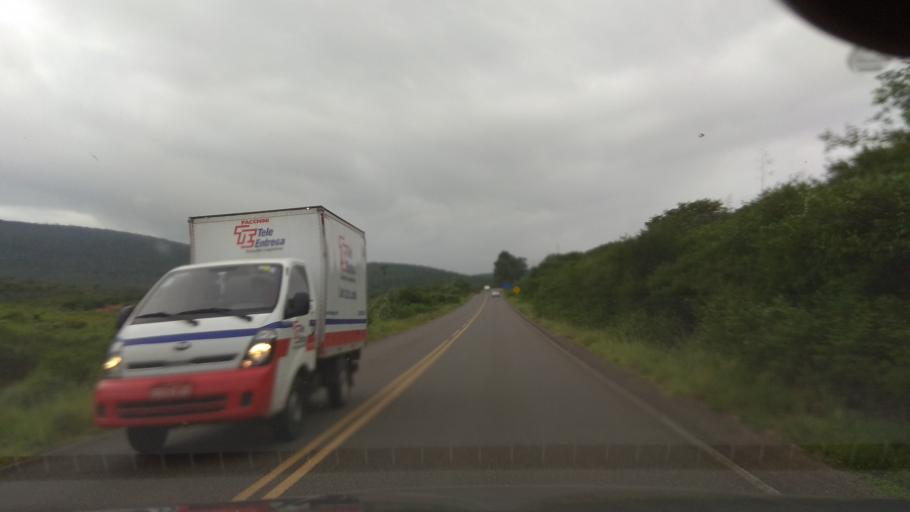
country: BR
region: Bahia
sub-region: Santa Ines
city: Santa Ines
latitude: -13.2748
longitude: -39.8092
